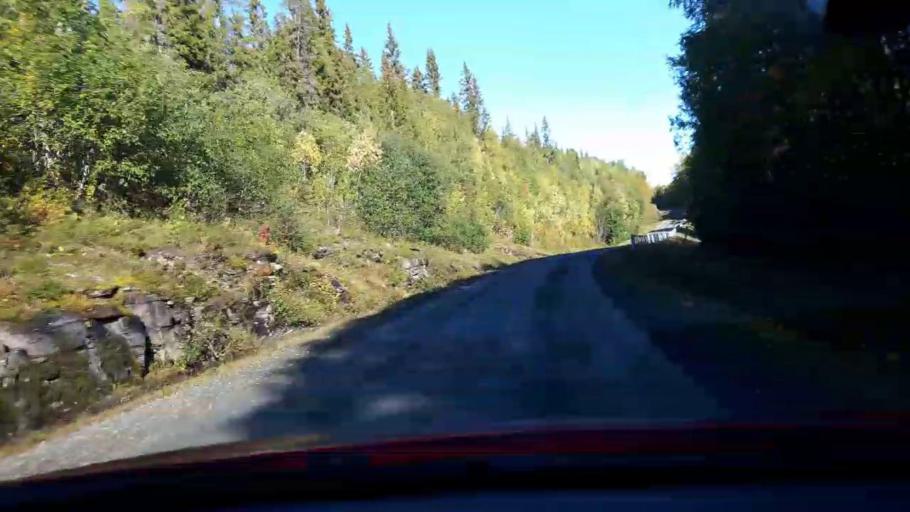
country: NO
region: Nord-Trondelag
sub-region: Lierne
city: Sandvika
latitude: 64.5696
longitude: 13.9040
